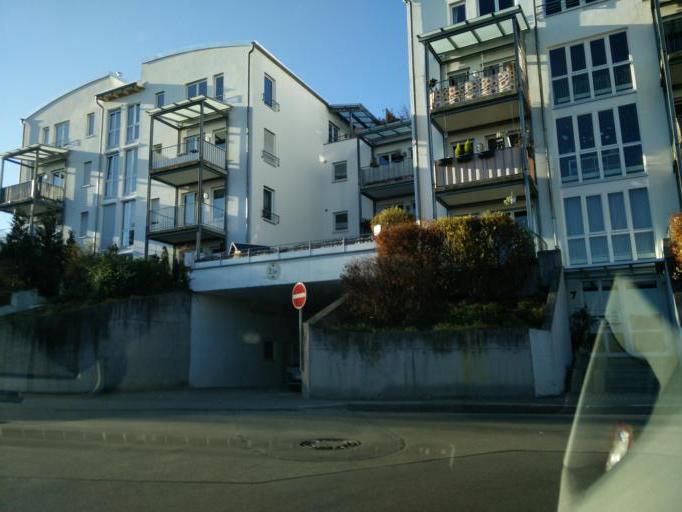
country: DE
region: Baden-Wuerttemberg
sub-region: Tuebingen Region
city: Gomaringen
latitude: 48.4541
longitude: 9.0977
